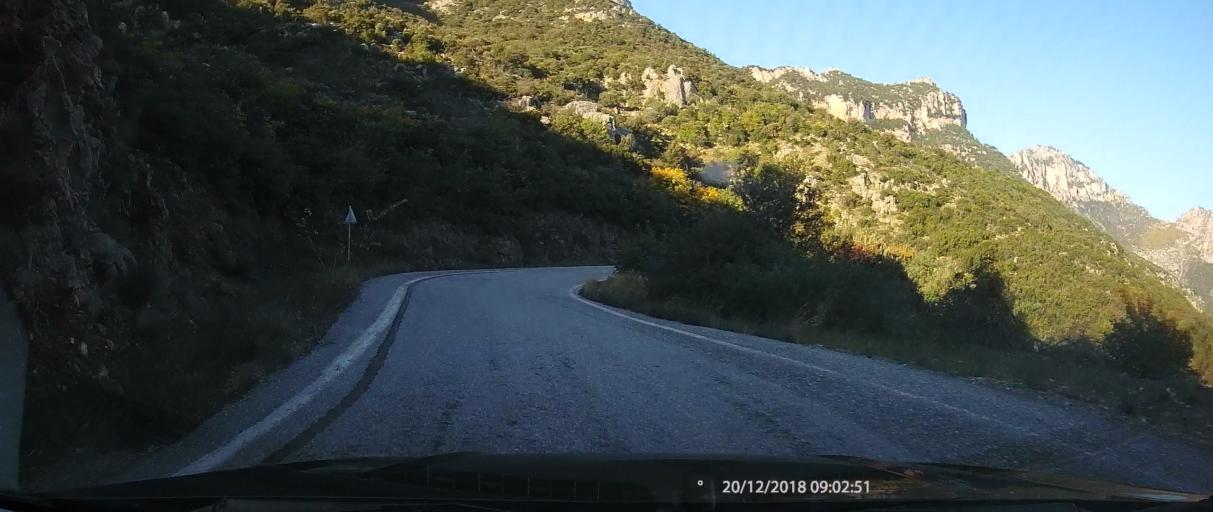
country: GR
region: Peloponnese
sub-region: Nomos Lakonias
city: Sykea
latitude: 36.9538
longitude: 22.9924
